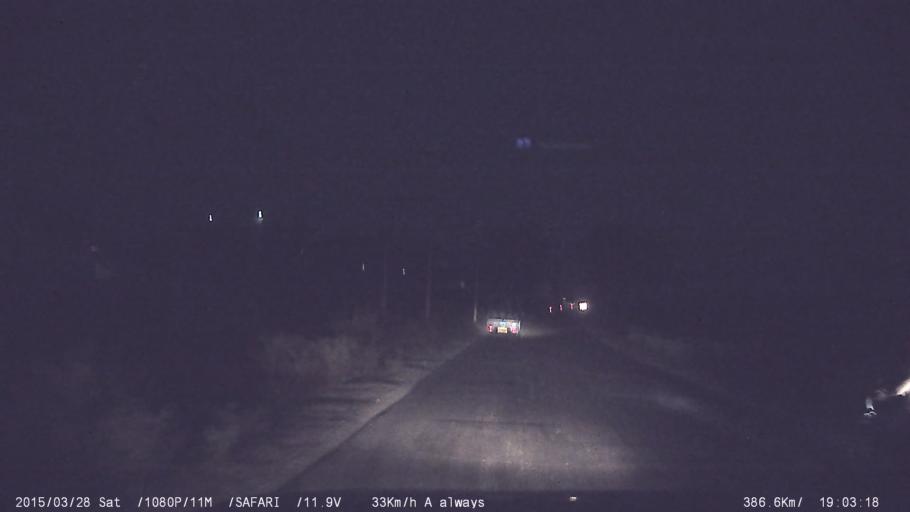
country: IN
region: Karnataka
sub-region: Mandya
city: Shrirangapattana
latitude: 12.3917
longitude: 76.5976
